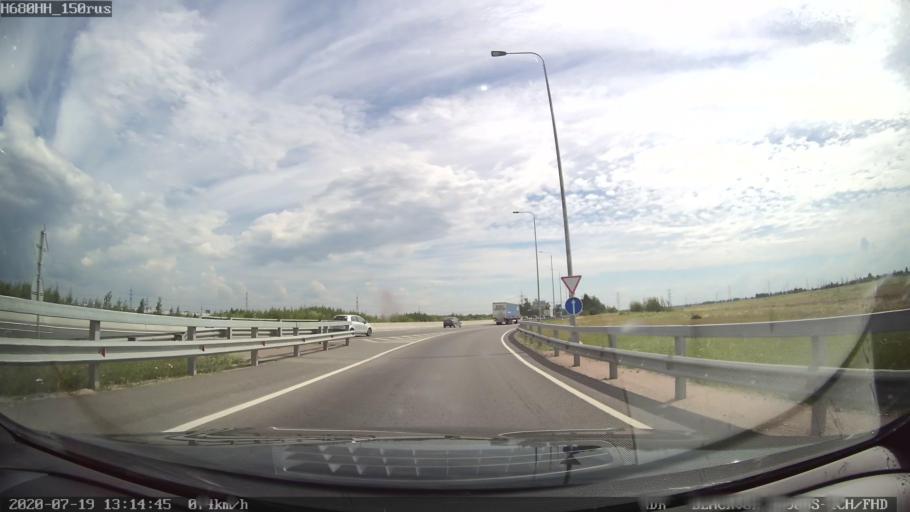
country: RU
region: St.-Petersburg
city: Kolpino
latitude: 59.7305
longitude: 30.5297
